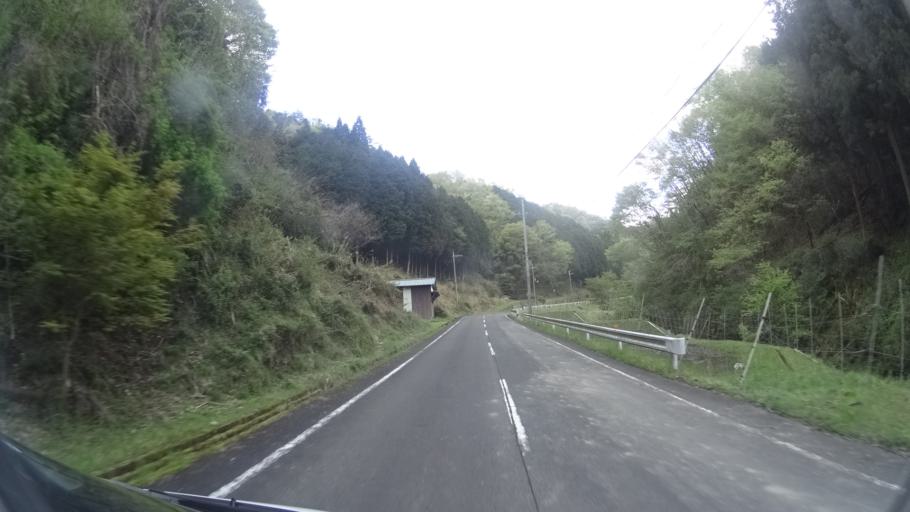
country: JP
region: Kyoto
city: Ayabe
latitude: 35.2553
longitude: 135.3139
